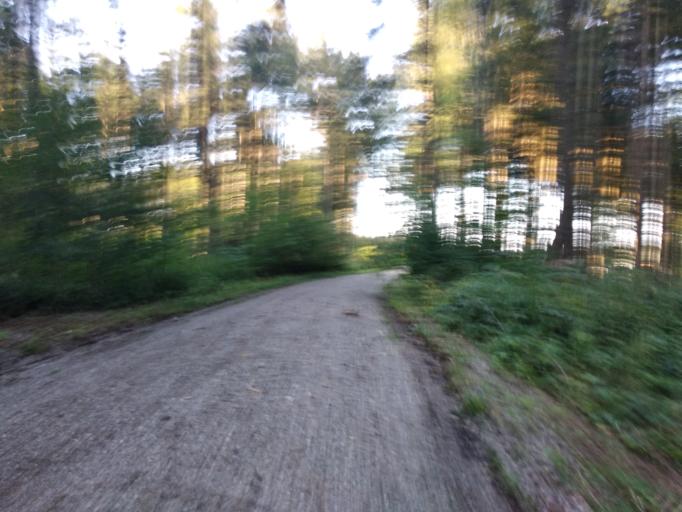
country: DE
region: Bavaria
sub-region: Swabia
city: Lautrach
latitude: 47.8867
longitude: 10.1021
